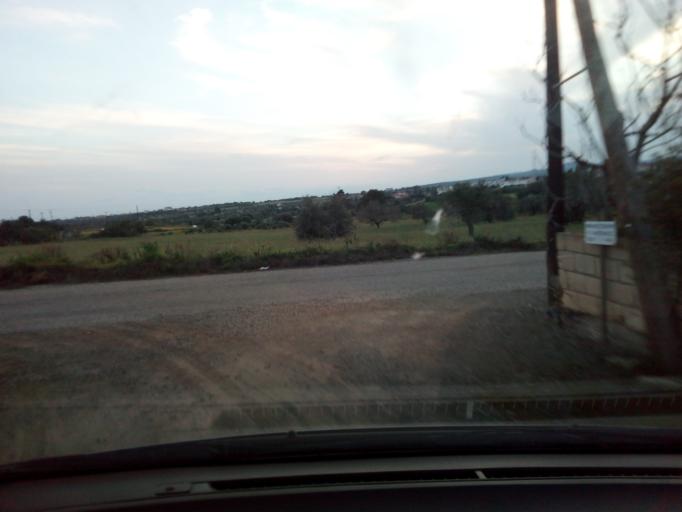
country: CY
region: Larnaka
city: Tersefanou
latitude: 34.7994
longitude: 33.4989
